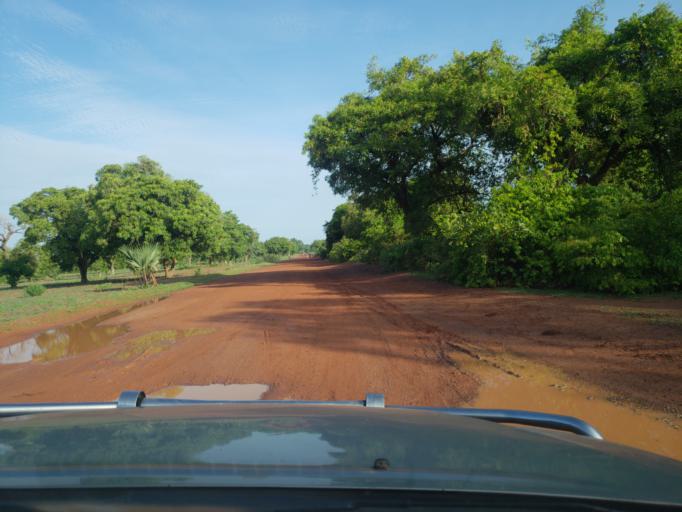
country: ML
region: Sikasso
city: Koutiala
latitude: 12.4228
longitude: -5.5882
